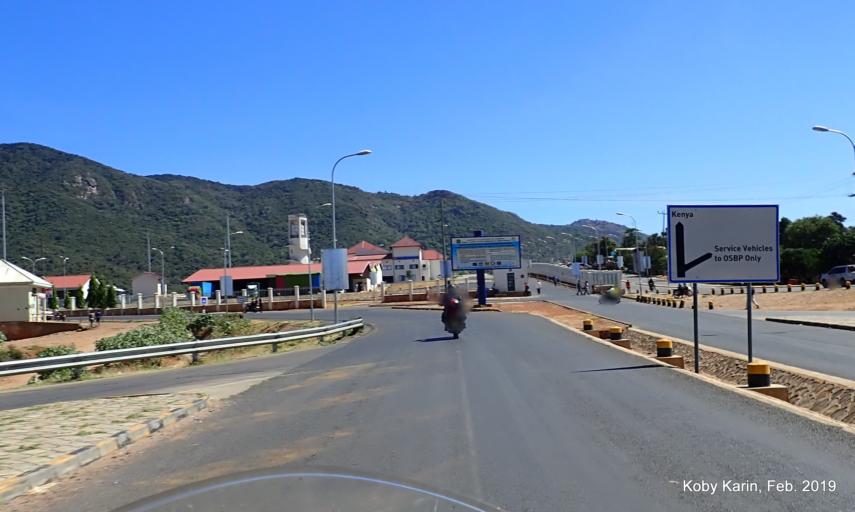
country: TZ
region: Arusha
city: Namanga
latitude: -2.5519
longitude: 36.7839
